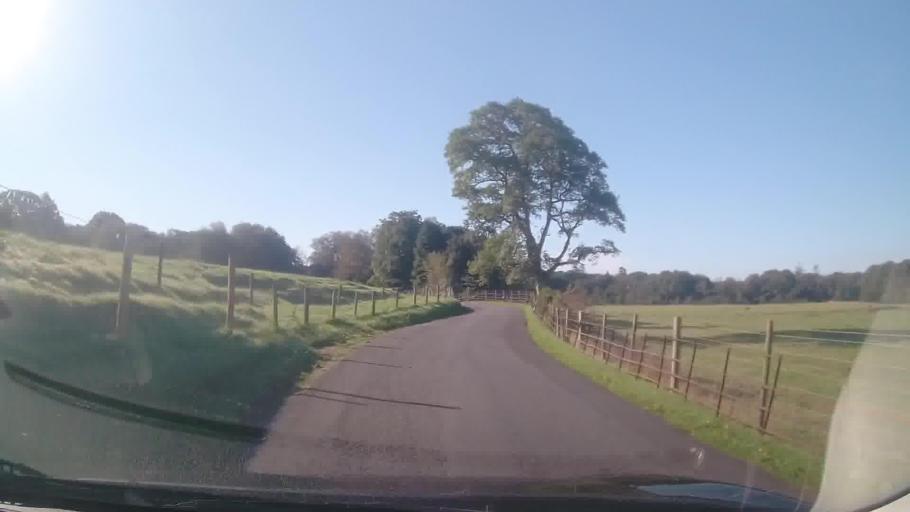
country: GB
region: England
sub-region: Cumbria
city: Seascale
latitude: 54.3969
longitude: -3.3788
